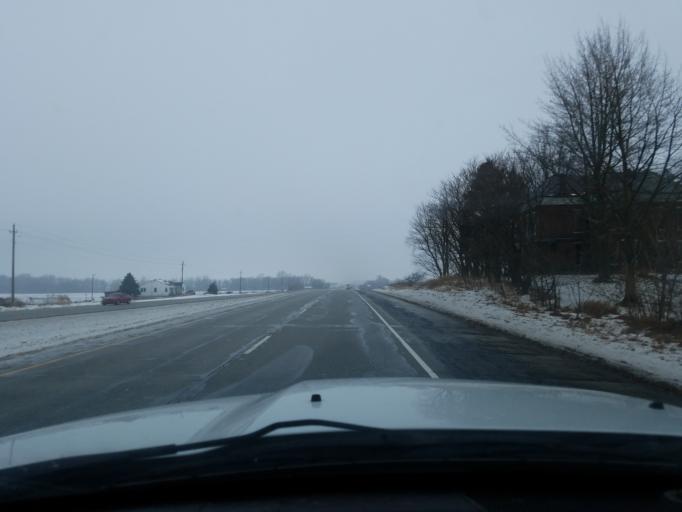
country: US
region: Indiana
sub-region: Miami County
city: Grissom Air Force Base
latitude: 40.6025
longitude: -86.1275
